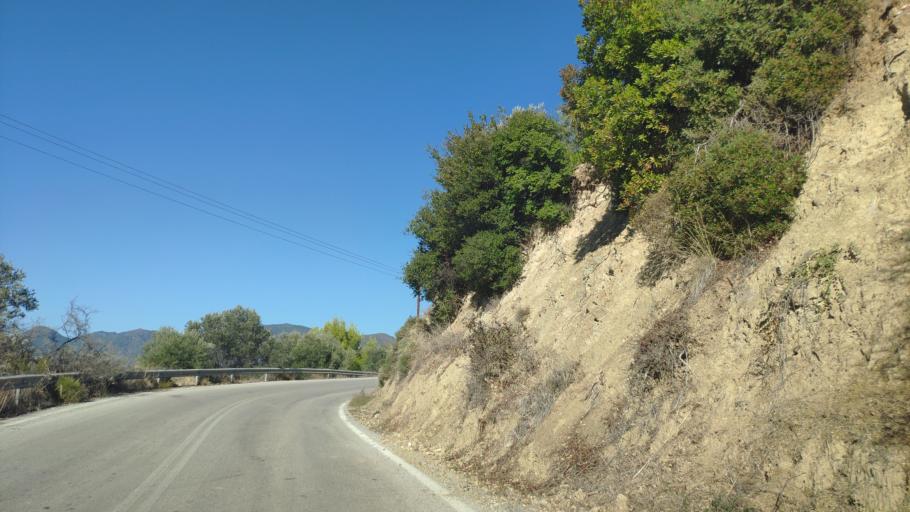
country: GR
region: Attica
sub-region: Nomos Piraios
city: Galatas
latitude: 37.5380
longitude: 23.3574
